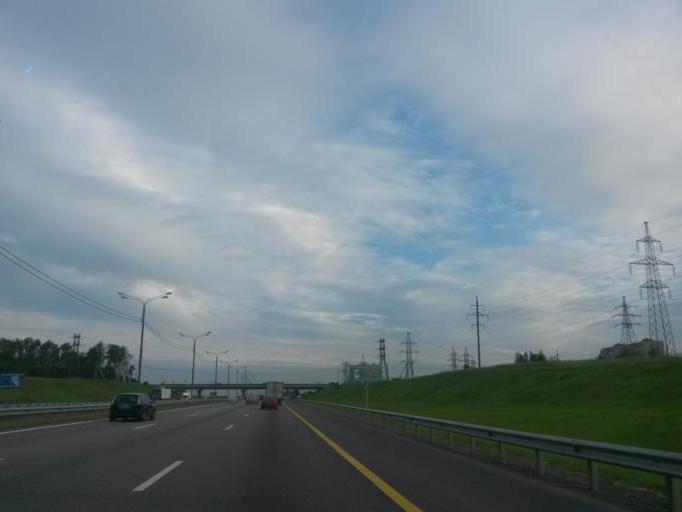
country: RU
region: Moskovskaya
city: Vostryakovo
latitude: 55.3809
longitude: 37.7775
